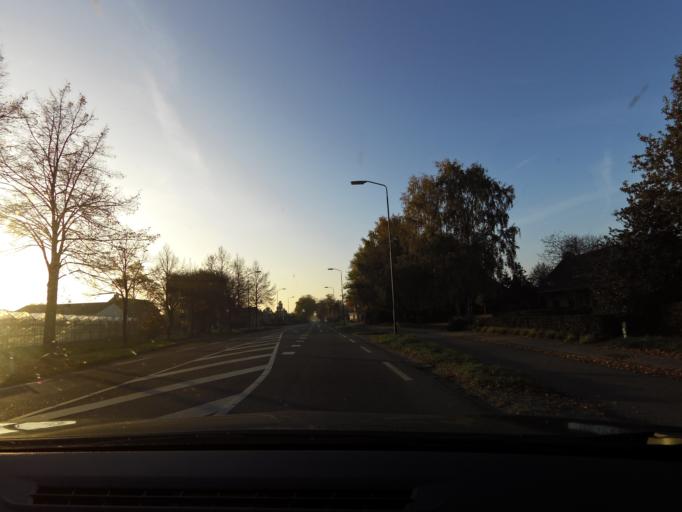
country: NL
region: North Brabant
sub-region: Gemeente Rucphen
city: Rucphen
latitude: 51.5867
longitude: 4.5699
